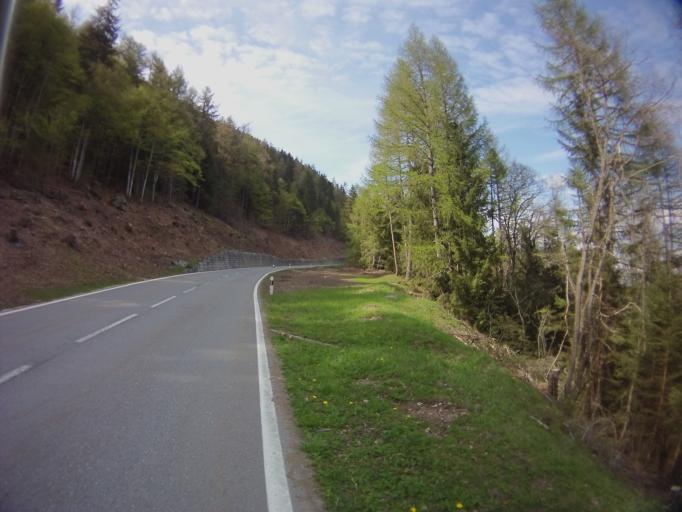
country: CH
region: Valais
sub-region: Martigny District
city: Martigny-Combe
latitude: 46.0674
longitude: 7.0203
